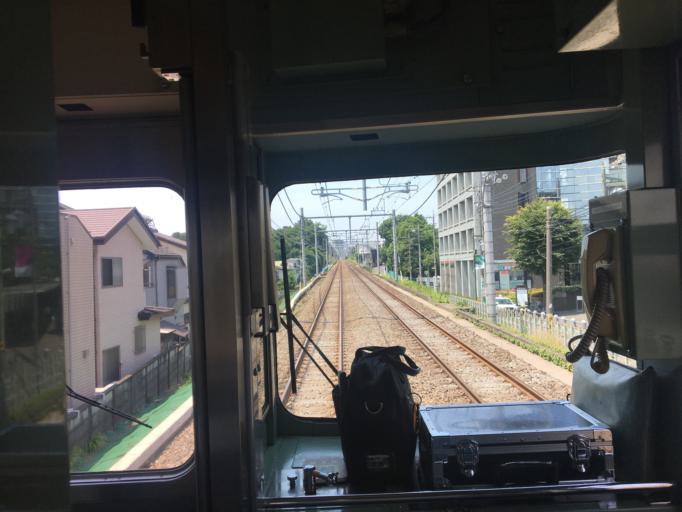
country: JP
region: Tokyo
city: Tanashicho
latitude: 35.7628
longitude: 139.5315
